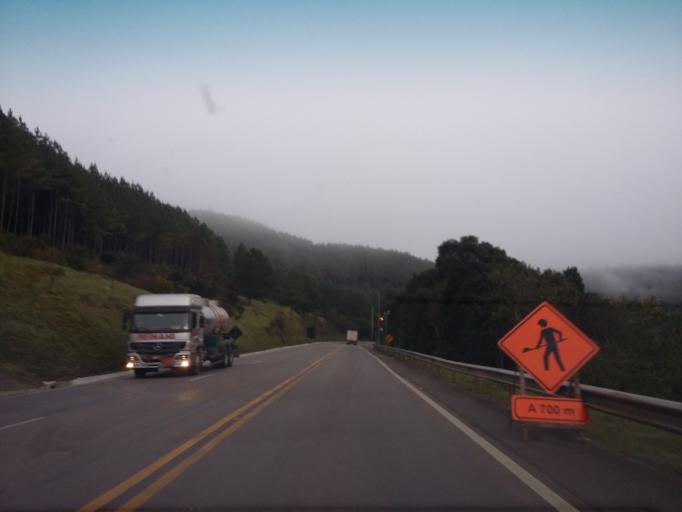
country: BR
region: Santa Catarina
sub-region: Curitibanos
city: Curitibanos
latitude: -27.2192
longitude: -50.4636
